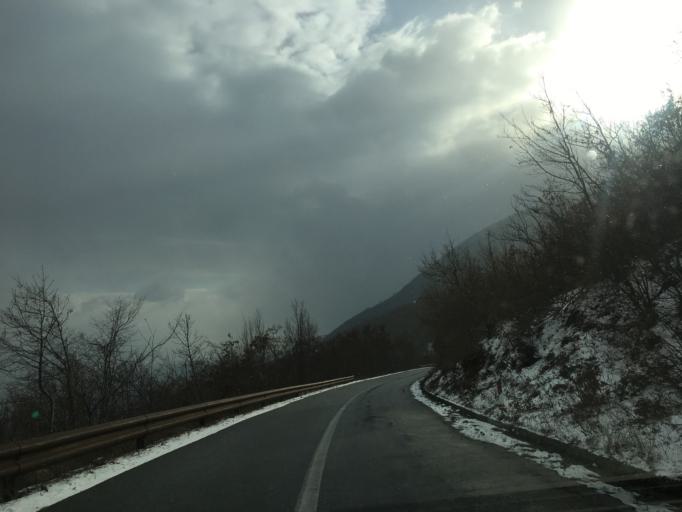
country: XK
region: Pec
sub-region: Komuna e Pejes
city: Dubova (Driloni)
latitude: 42.7563
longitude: 20.3013
